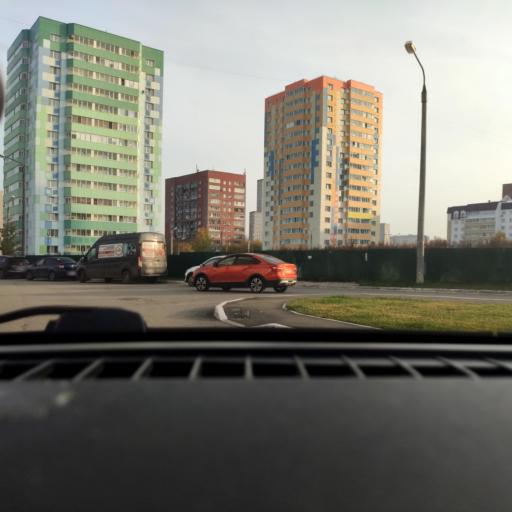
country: RU
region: Perm
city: Perm
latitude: 57.9985
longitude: 56.2016
